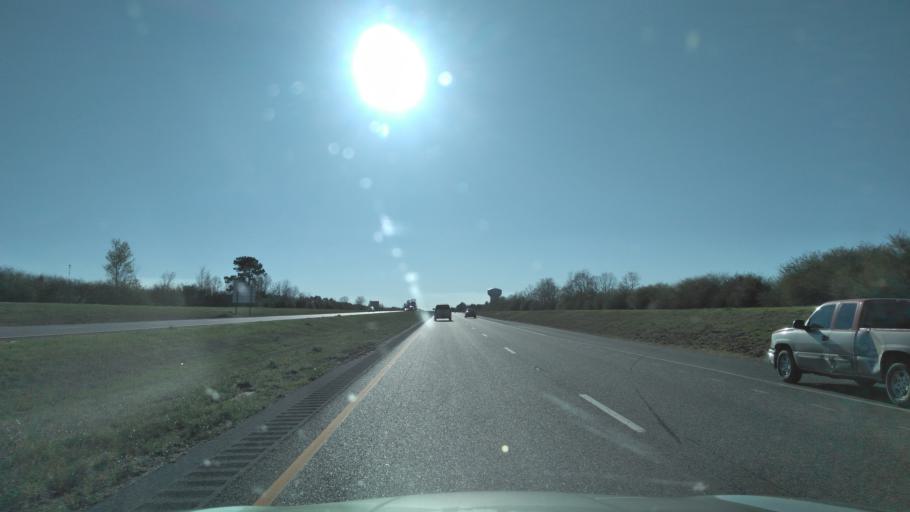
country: US
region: Alabama
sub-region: Escambia County
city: Atmore
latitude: 31.1096
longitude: -87.4783
